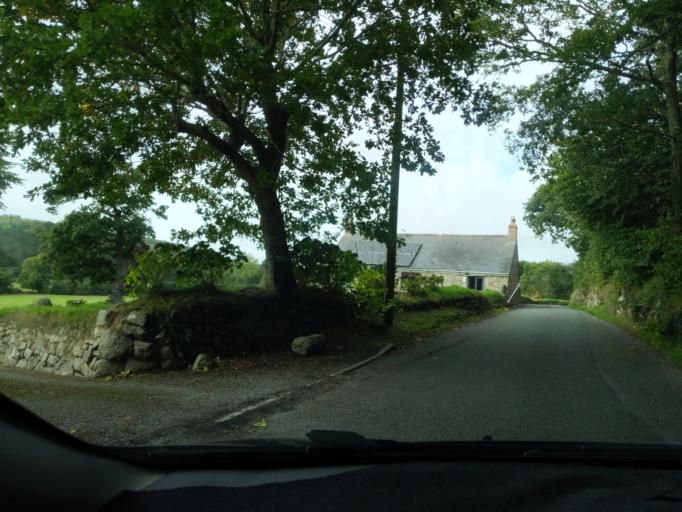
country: GB
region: England
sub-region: Cornwall
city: Lostwithiel
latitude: 50.4001
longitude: -4.6941
